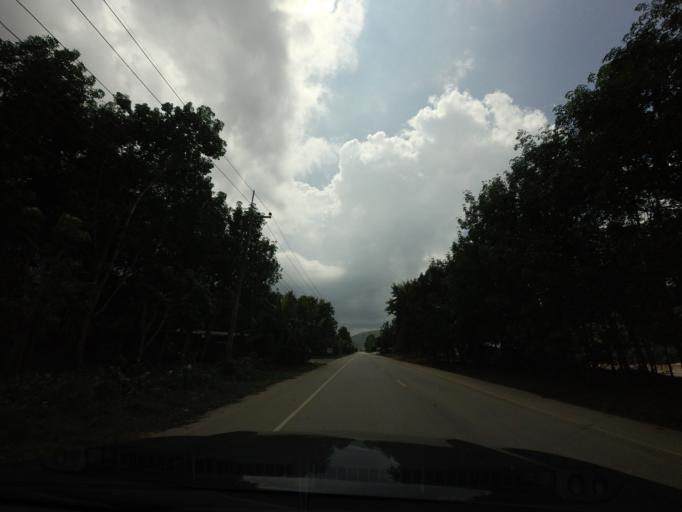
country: LA
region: Vientiane
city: Muang Sanakham
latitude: 17.9952
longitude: 101.7517
